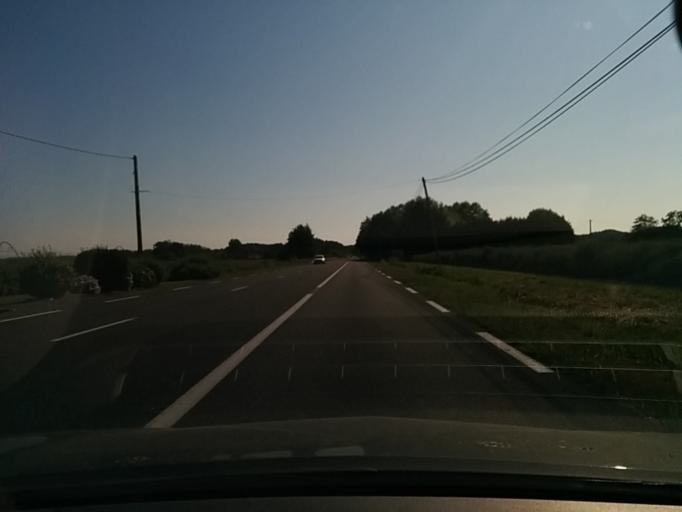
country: FR
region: Aquitaine
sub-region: Departement des Landes
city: Benesse-Maremne
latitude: 43.6216
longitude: -1.3851
